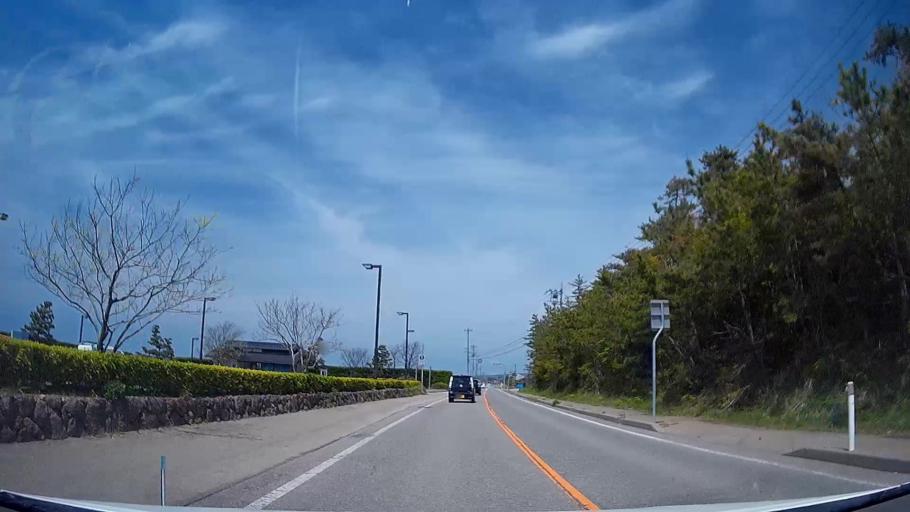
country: JP
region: Ishikawa
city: Hakui
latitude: 36.9329
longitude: 136.7564
